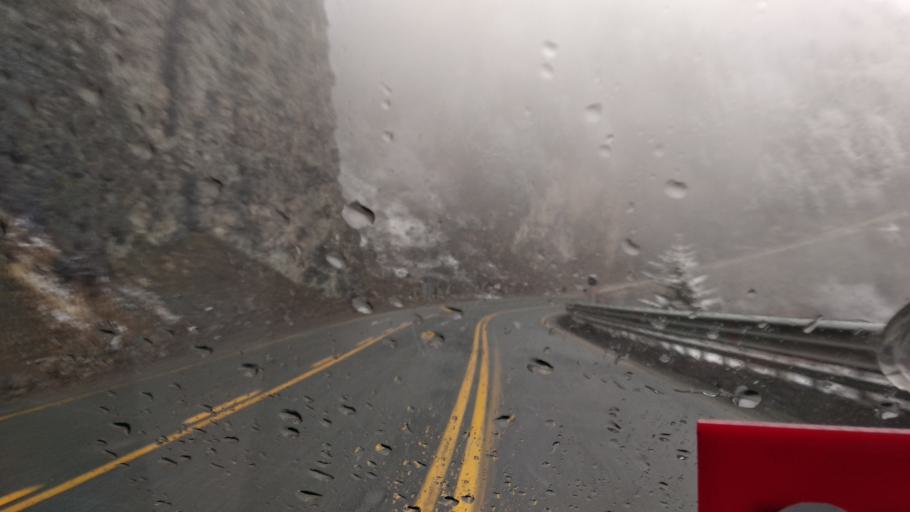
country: TR
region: Gumushane
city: Yaglidere
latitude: 40.6989
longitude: 39.4777
